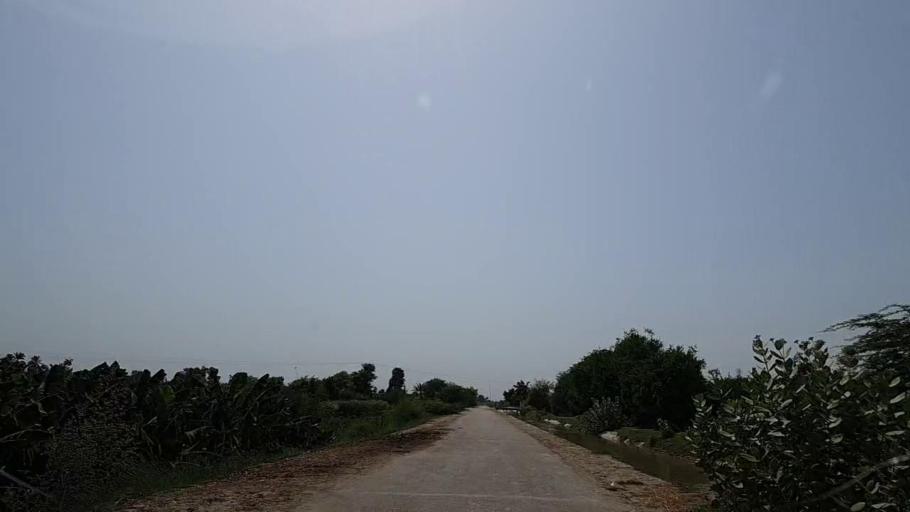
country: PK
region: Sindh
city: Kandiaro
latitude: 27.0504
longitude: 68.1559
